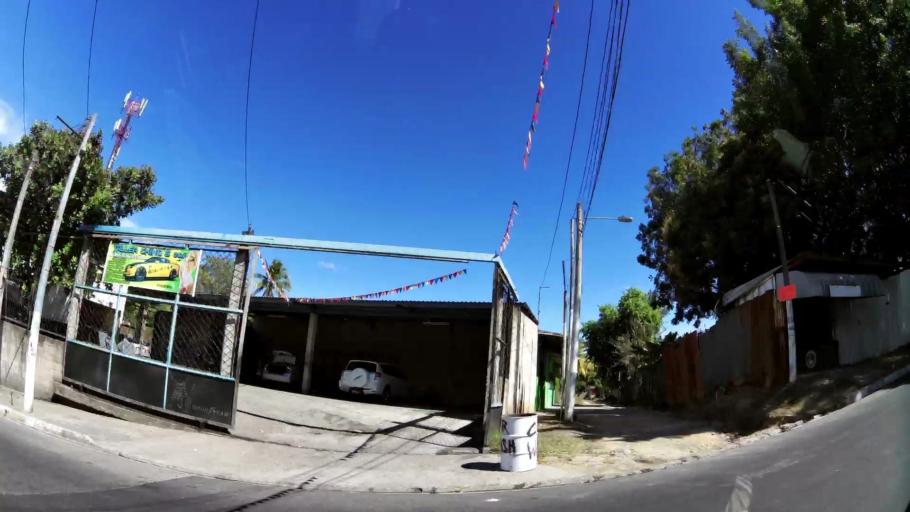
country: SV
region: San Salvador
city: Apopa
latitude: 13.8107
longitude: -89.1795
